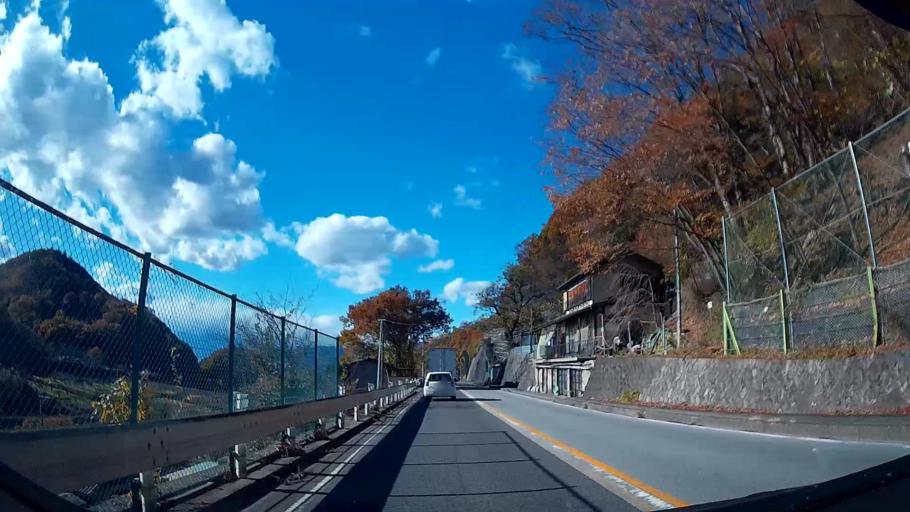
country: JP
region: Yamanashi
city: Enzan
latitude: 35.6524
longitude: 138.7537
